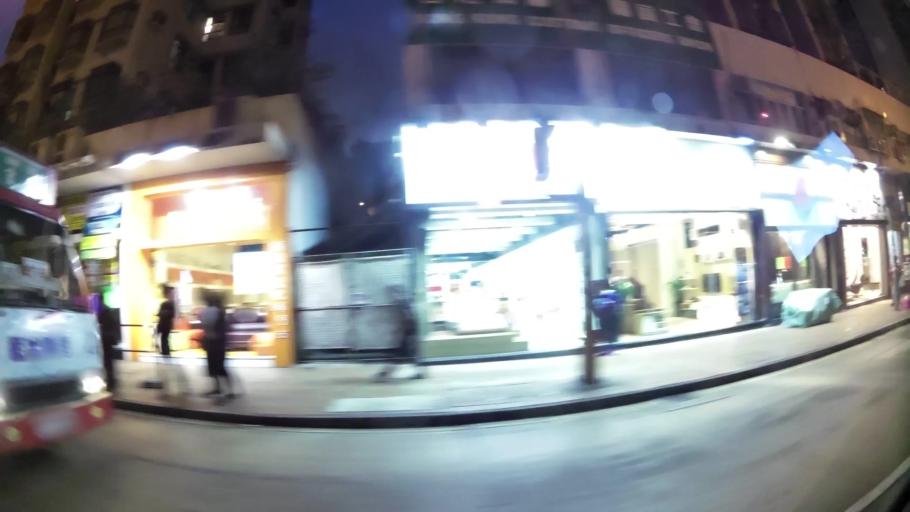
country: HK
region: Kowloon City
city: Kowloon
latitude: 22.3121
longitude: 114.1858
